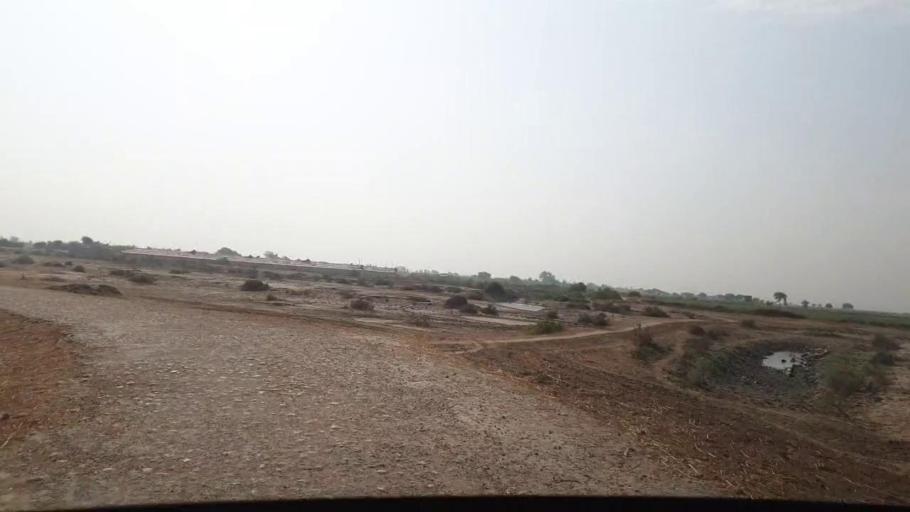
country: PK
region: Sindh
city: Chuhar Jamali
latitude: 24.3815
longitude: 67.9390
